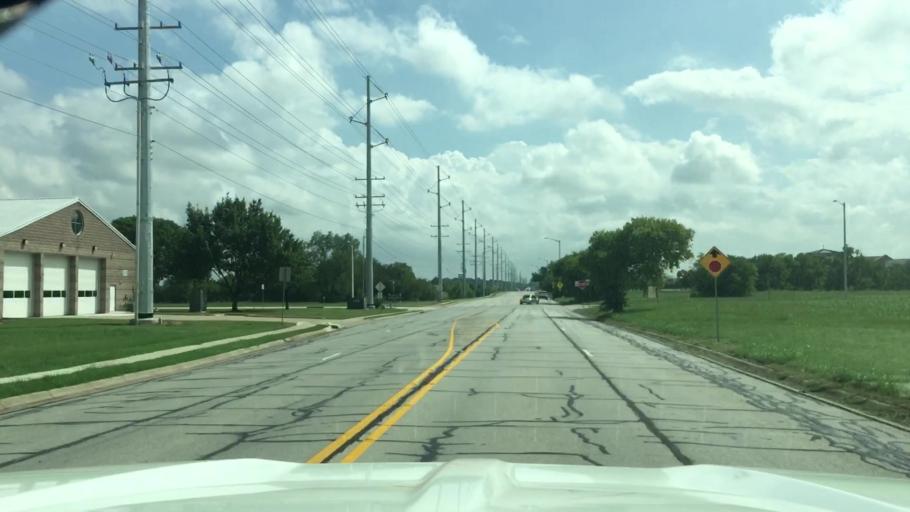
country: US
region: Texas
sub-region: Denton County
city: Denton
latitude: 33.2407
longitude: -97.1608
